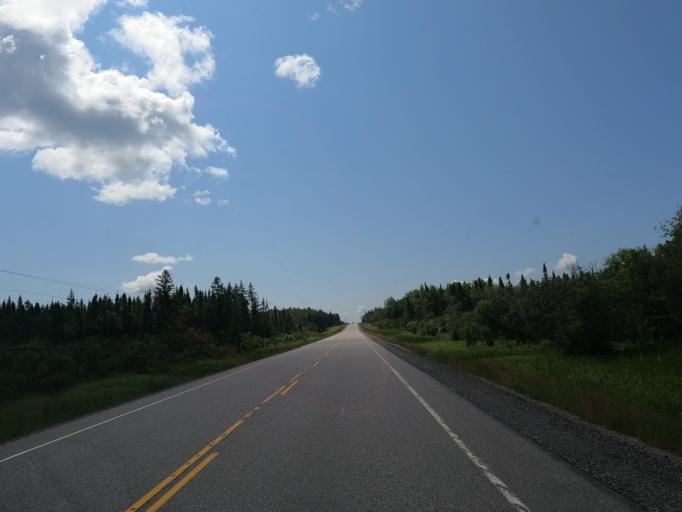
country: CA
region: Ontario
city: Dryden
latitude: 49.9144
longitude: -93.3595
